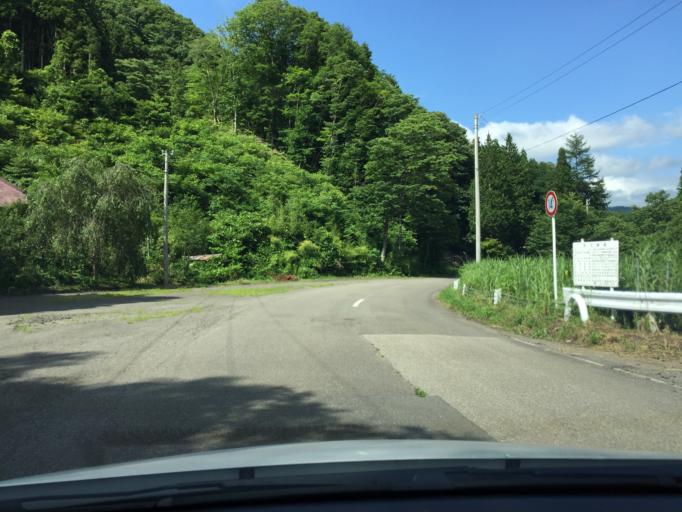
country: JP
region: Fukushima
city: Inawashiro
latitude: 37.2955
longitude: 140.0679
